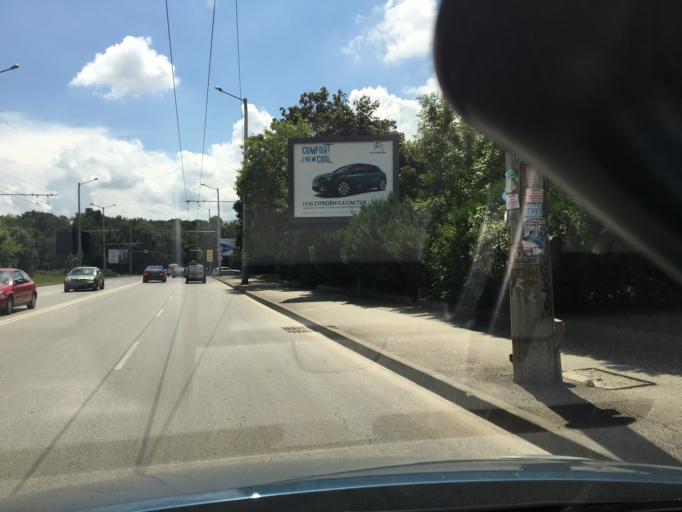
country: BG
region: Sofia-Capital
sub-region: Stolichna Obshtina
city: Sofia
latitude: 42.6746
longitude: 23.3038
